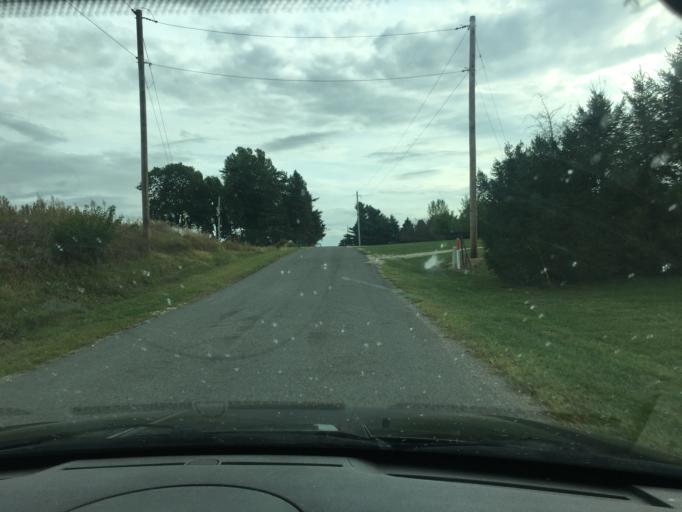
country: US
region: Ohio
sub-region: Logan County
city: Bellefontaine
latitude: 40.3277
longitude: -83.8056
